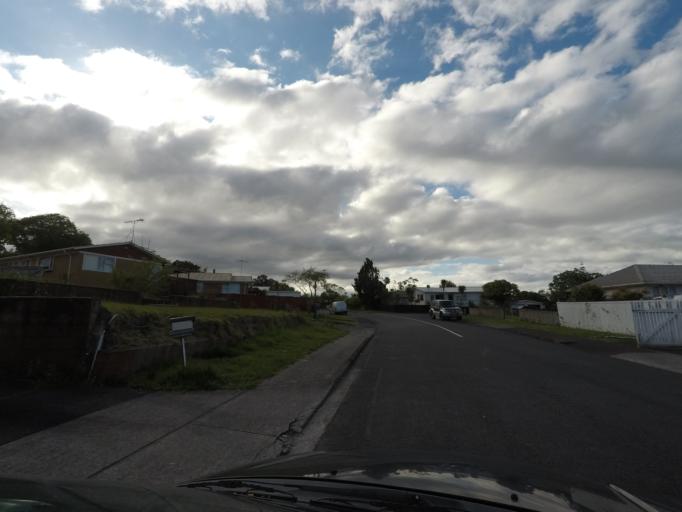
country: NZ
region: Auckland
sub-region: Auckland
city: Rosebank
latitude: -36.8833
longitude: 174.6534
